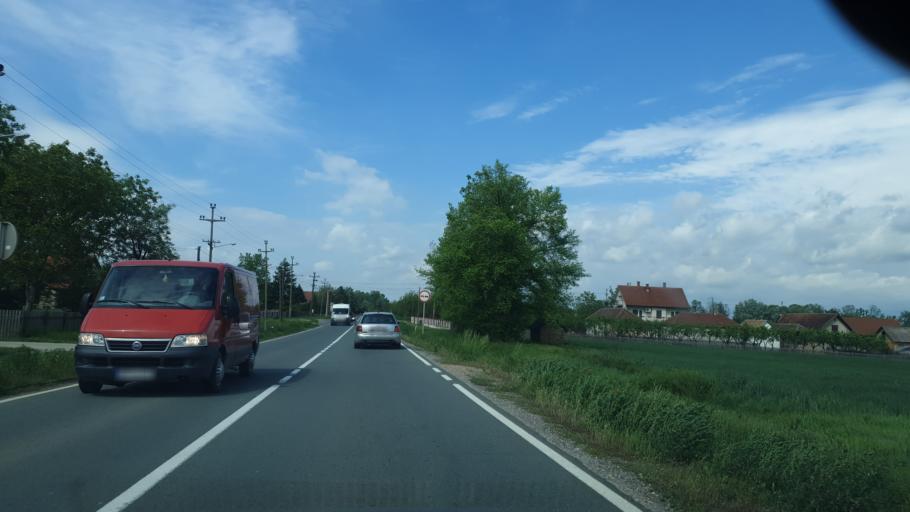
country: RS
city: Stubline
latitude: 44.6002
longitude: 20.1479
